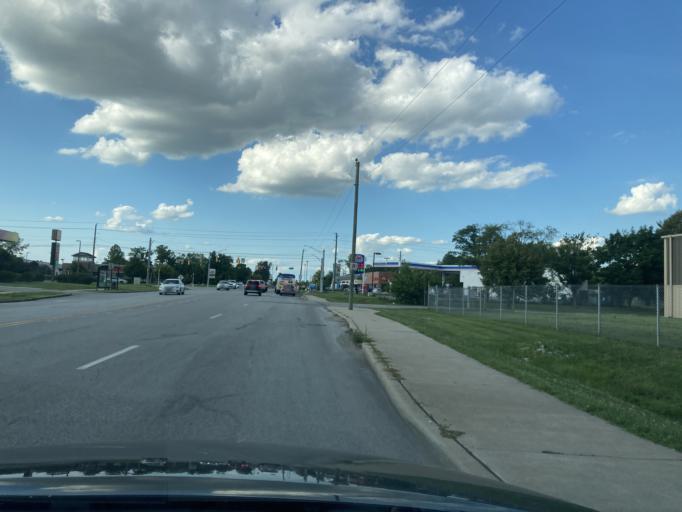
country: US
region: Indiana
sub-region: Boone County
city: Zionsville
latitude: 39.8809
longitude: -86.2442
